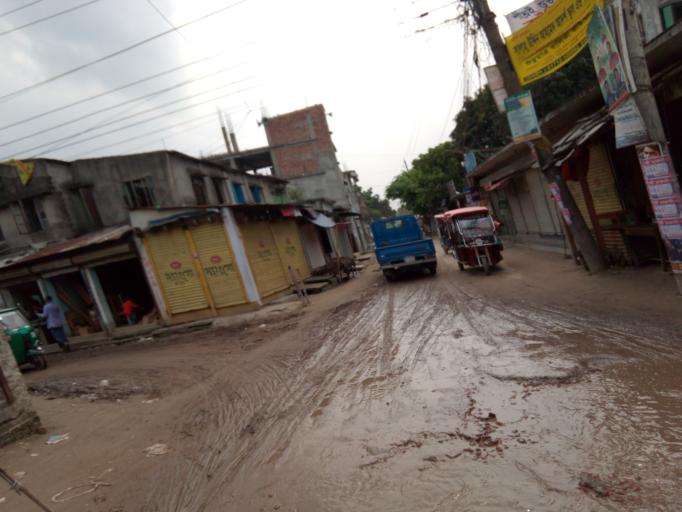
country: BD
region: Dhaka
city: Paltan
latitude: 23.7102
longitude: 90.4822
